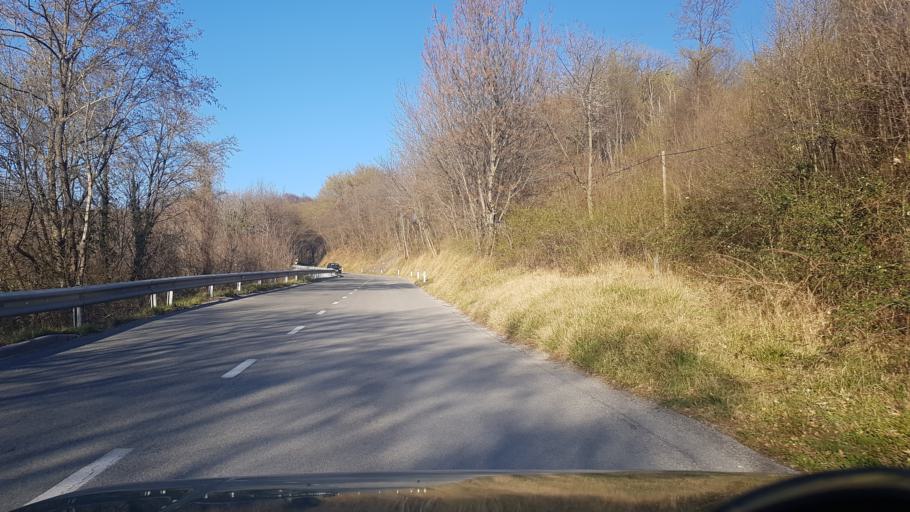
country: IT
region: Friuli Venezia Giulia
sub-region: Provincia di Gorizia
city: San Floriano del Collio
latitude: 46.0127
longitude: 13.5713
